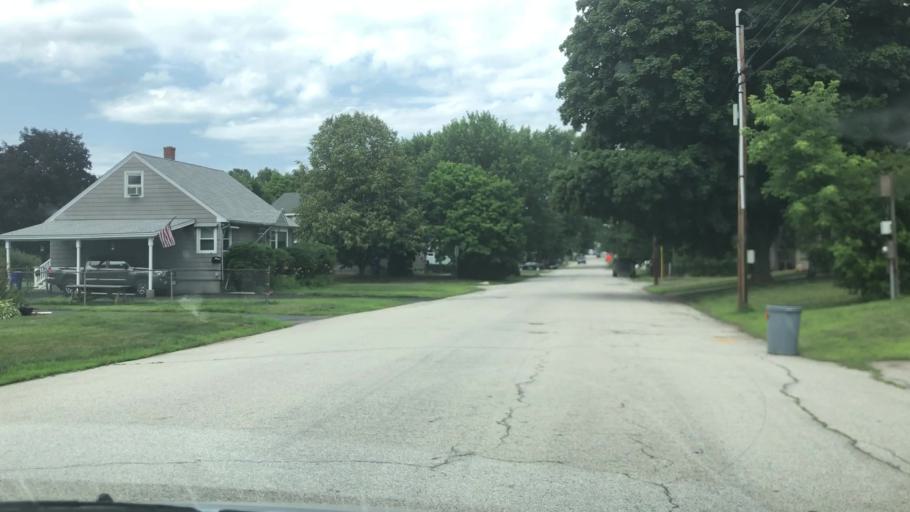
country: US
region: New Hampshire
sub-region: Hillsborough County
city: Manchester
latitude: 42.9775
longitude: -71.4333
